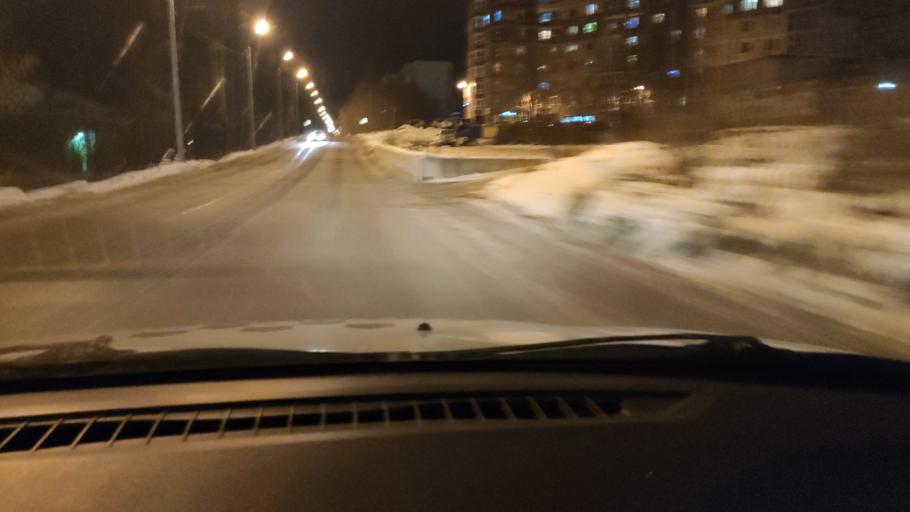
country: RU
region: Perm
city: Perm
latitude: 58.1019
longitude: 56.3079
